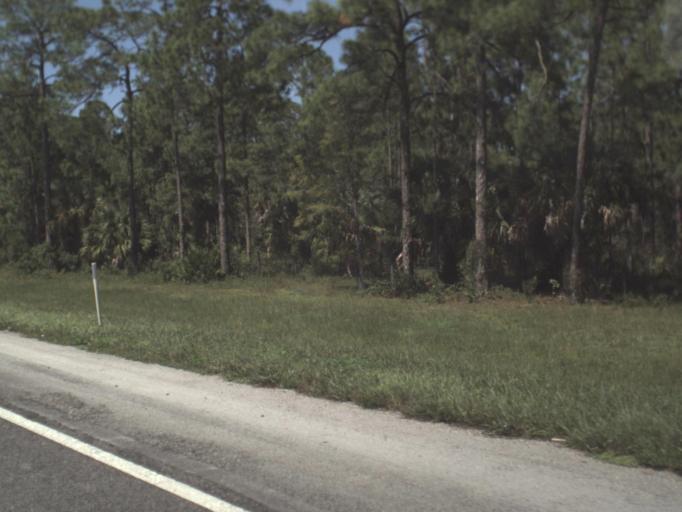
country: US
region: Florida
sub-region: Collier County
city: Golden Gate
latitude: 26.1628
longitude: -81.6949
